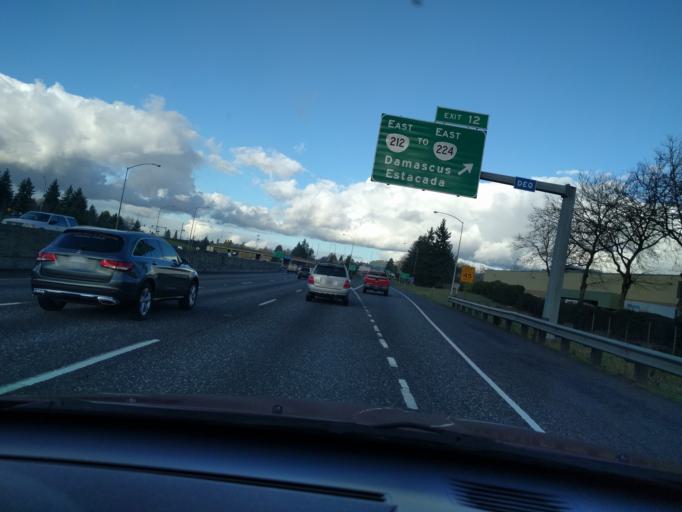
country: US
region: Oregon
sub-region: Clackamas County
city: Clackamas
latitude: 45.4041
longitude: -122.5714
